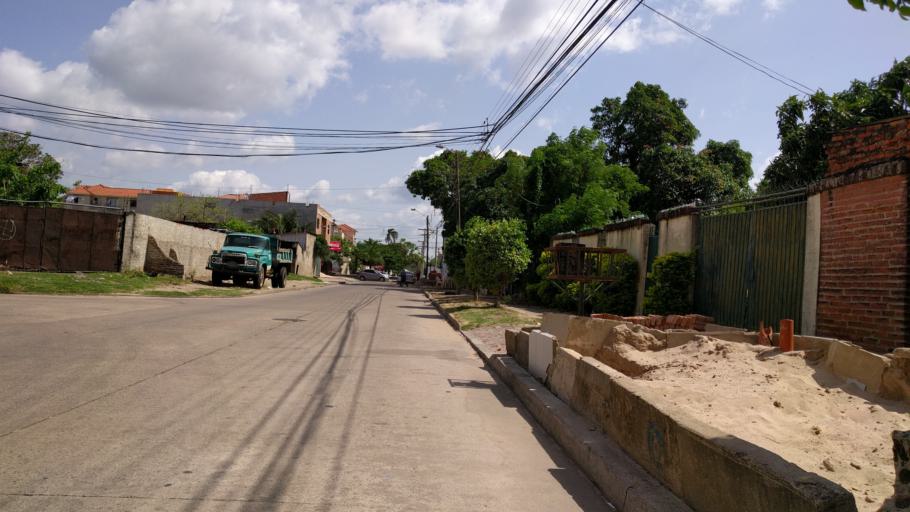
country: BO
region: Santa Cruz
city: Santa Cruz de la Sierra
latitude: -17.7787
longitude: -63.2125
